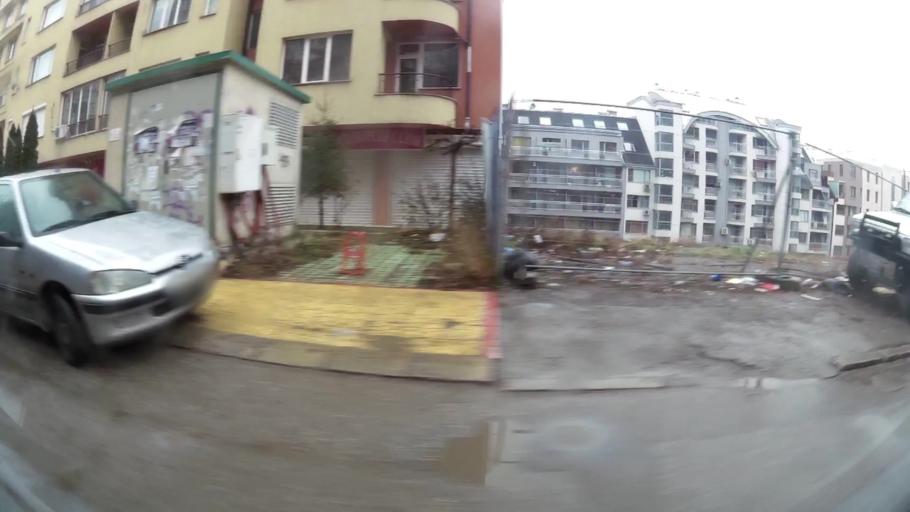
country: BG
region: Sofia-Capital
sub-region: Stolichna Obshtina
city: Sofia
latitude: 42.6400
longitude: 23.3659
